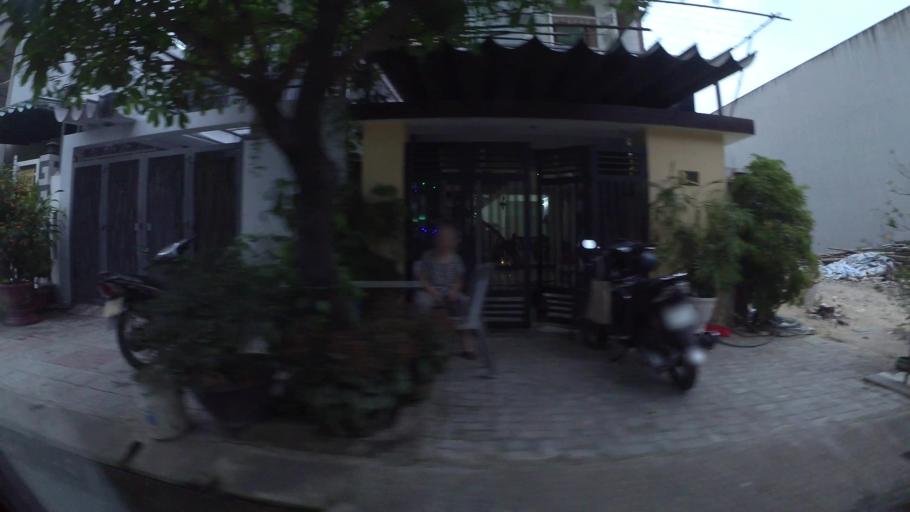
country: VN
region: Da Nang
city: Thanh Khe
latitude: 16.0470
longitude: 108.1760
